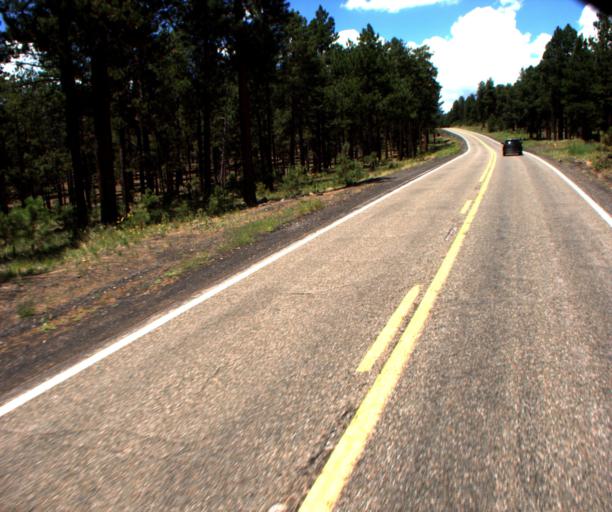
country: US
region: Arizona
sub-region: Coconino County
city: Flagstaff
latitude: 35.3032
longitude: -111.7682
